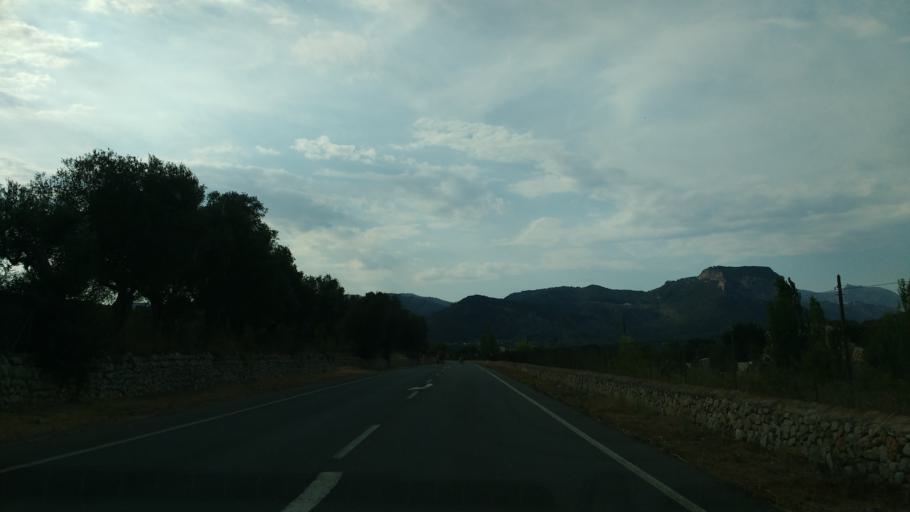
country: ES
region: Balearic Islands
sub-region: Illes Balears
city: Consell
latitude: 39.6873
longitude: 2.8077
